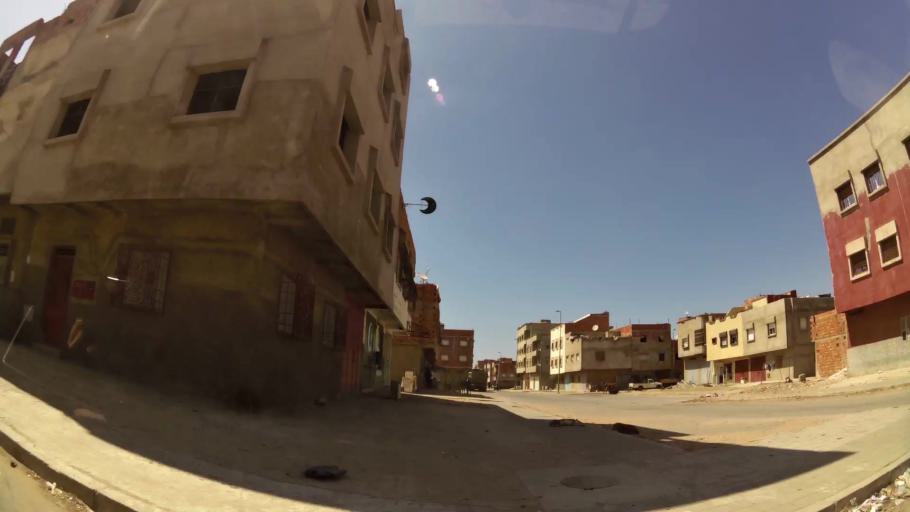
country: MA
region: Gharb-Chrarda-Beni Hssen
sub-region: Kenitra Province
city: Kenitra
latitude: 34.2270
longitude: -6.5456
